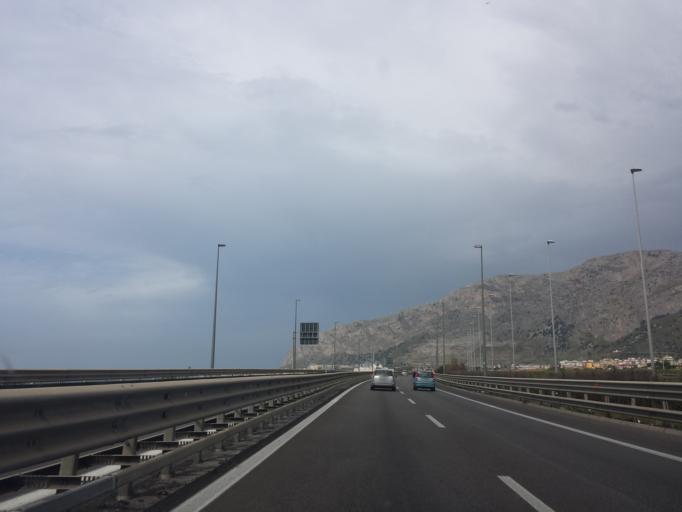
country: IT
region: Sicily
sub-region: Palermo
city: Capaci
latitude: 38.1774
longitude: 13.2222
